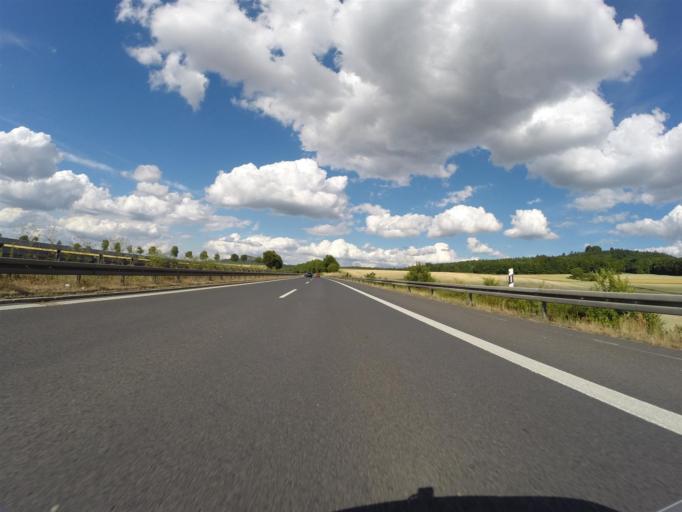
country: DE
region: Bavaria
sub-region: Upper Franconia
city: Ebensfeld
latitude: 50.0674
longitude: 10.9831
